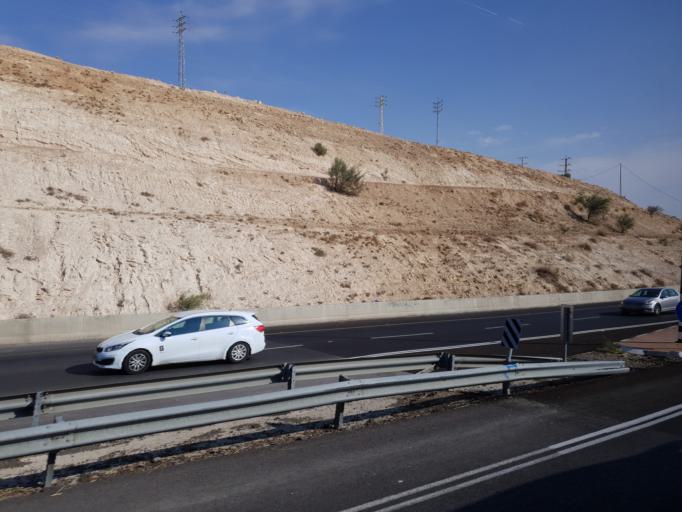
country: PS
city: Az Za`ayyim
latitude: 31.7996
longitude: 35.3101
